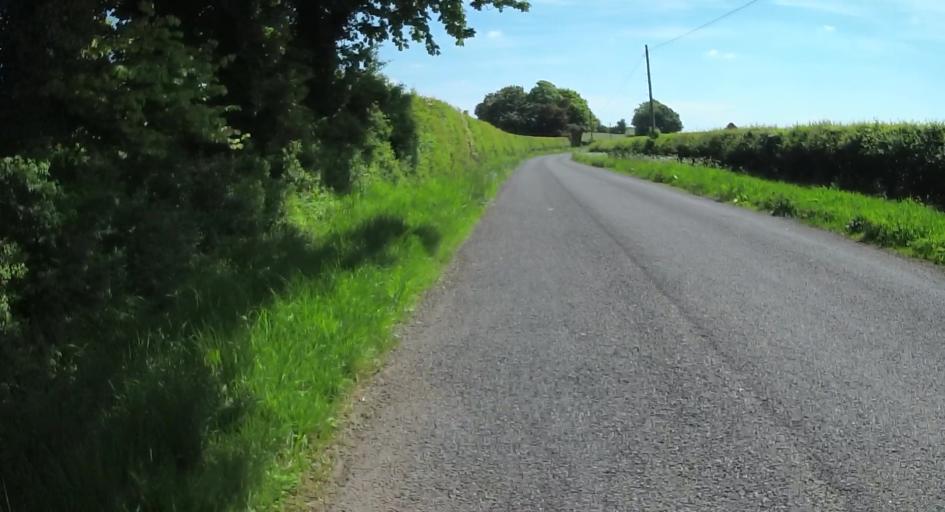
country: GB
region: England
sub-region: Hampshire
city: Four Marks
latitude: 51.1633
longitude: -1.1358
